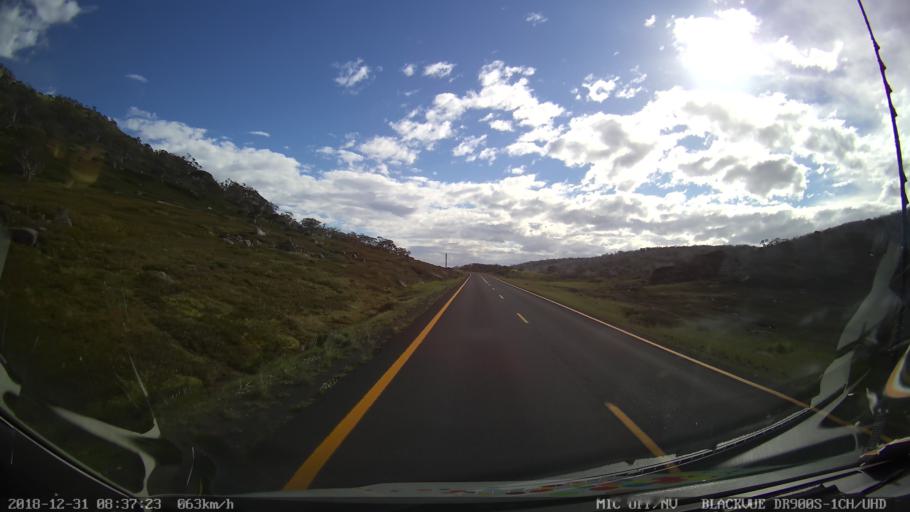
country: AU
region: New South Wales
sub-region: Snowy River
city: Jindabyne
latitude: -36.4196
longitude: 148.3848
